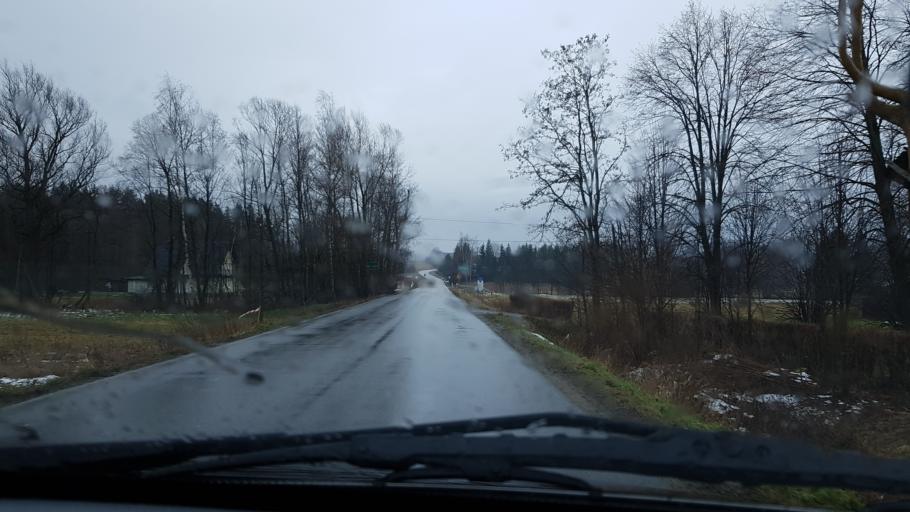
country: PL
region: Lesser Poland Voivodeship
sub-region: Powiat nowotarski
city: Spytkowice
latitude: 49.5951
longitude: 19.8374
